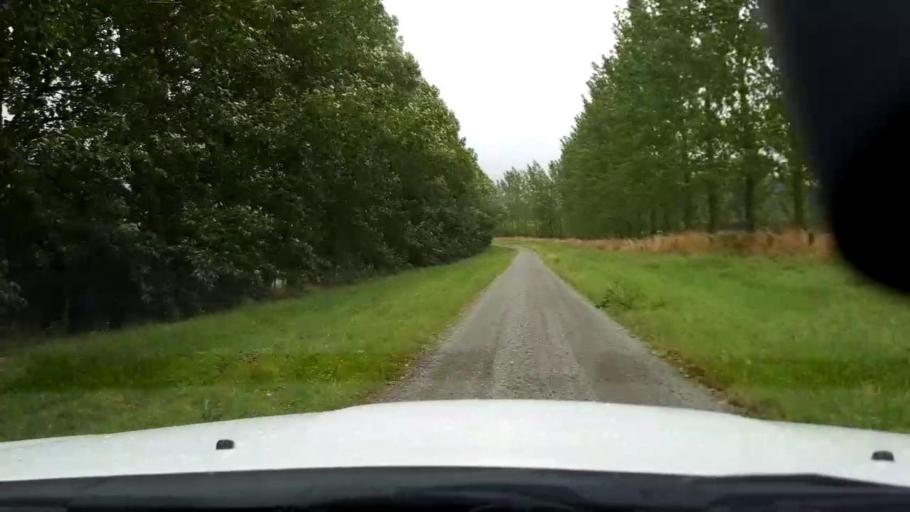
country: NZ
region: Canterbury
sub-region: Timaru District
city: Pleasant Point
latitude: -44.1038
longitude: 171.1350
